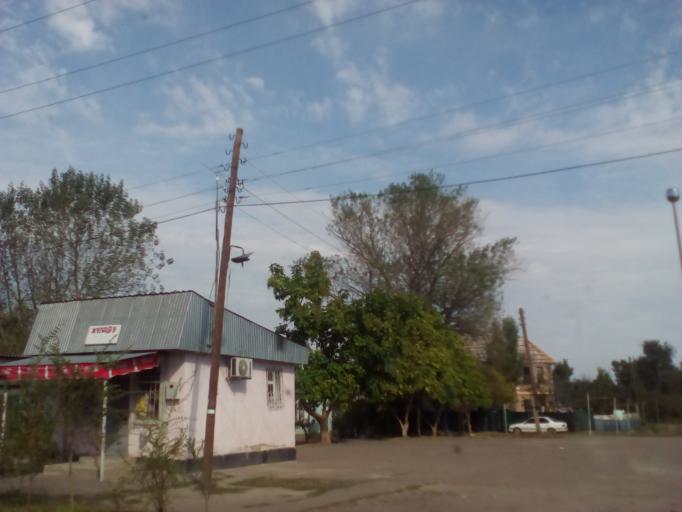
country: KZ
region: Almaty Oblysy
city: Burunday
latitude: 43.1681
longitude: 76.4045
